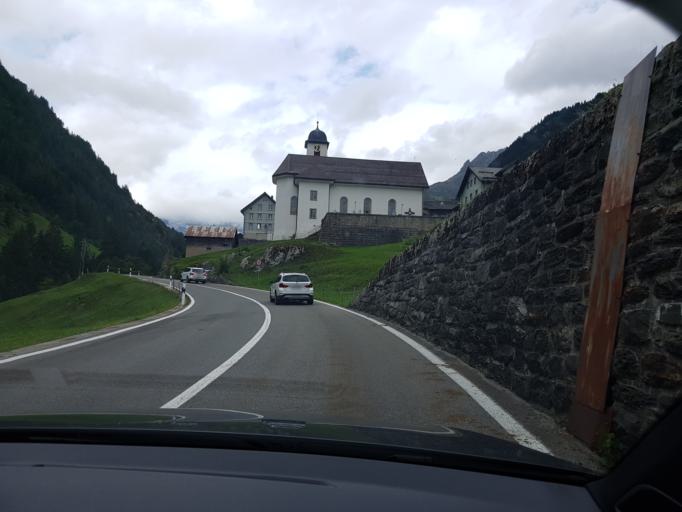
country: CH
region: Uri
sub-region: Uri
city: Andermatt
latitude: 46.7247
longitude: 8.5544
